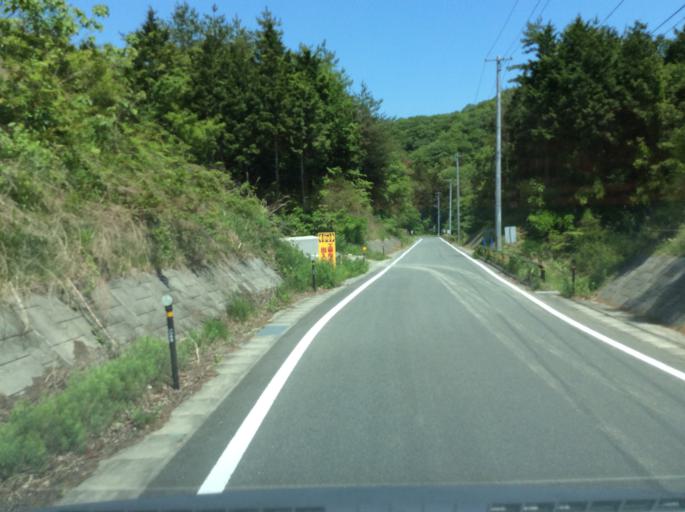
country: JP
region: Fukushima
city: Iwaki
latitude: 37.0043
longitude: 140.9356
